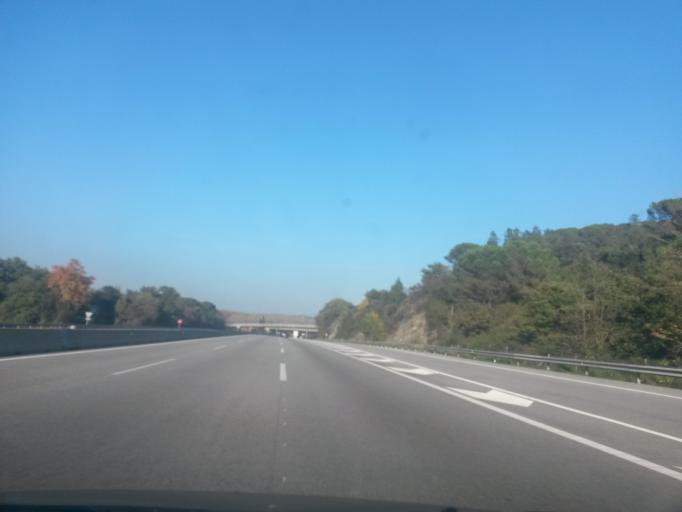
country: ES
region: Catalonia
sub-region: Provincia de Girona
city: Hostalric
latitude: 41.7360
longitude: 2.6402
